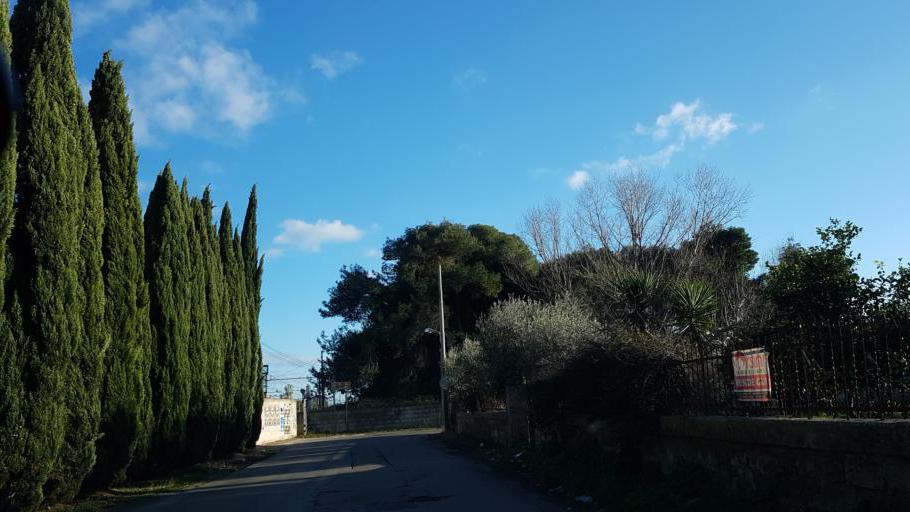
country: IT
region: Apulia
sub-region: Provincia di Lecce
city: Squinzano
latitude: 40.4425
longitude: 18.0423
